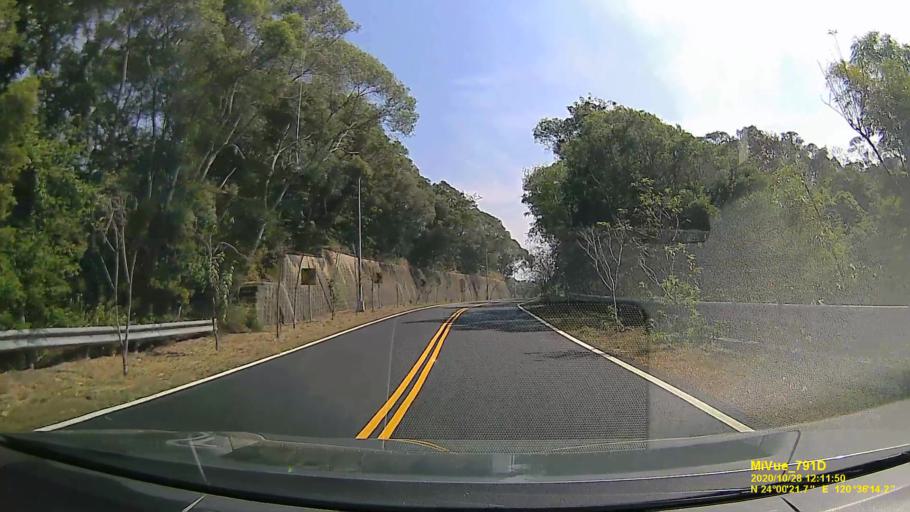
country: TW
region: Taiwan
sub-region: Changhua
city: Chang-hua
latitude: 24.0059
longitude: 120.6040
